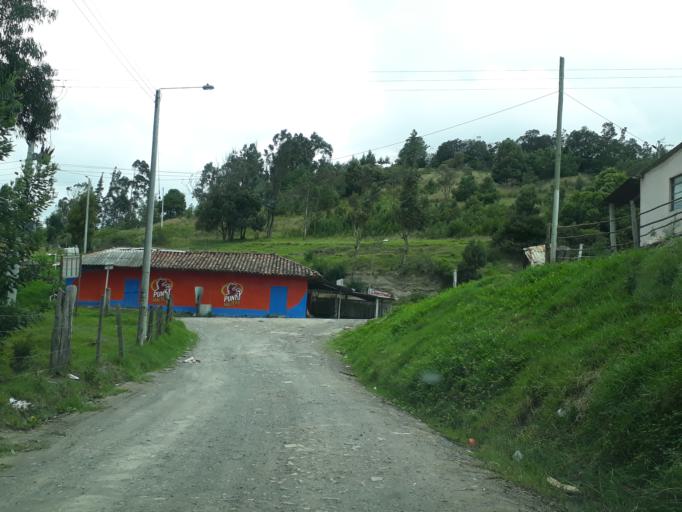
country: CO
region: Cundinamarca
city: Simijaca
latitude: 5.5525
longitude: -73.8231
